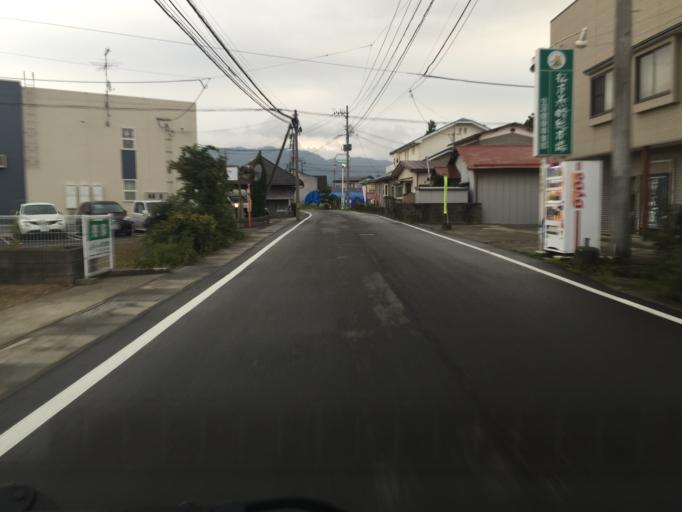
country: JP
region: Fukushima
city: Kitakata
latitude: 37.4954
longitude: 139.9040
